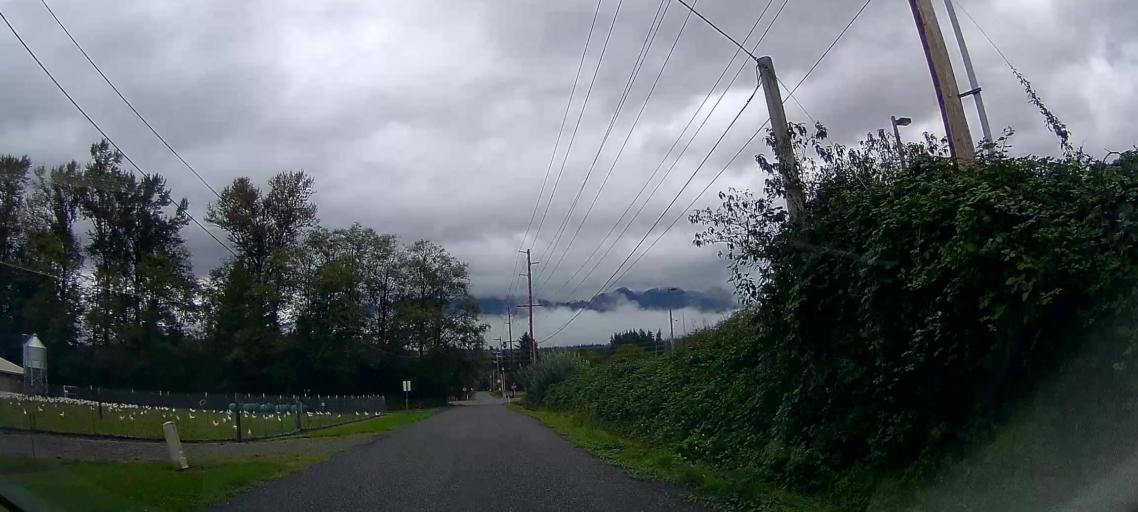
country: US
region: Washington
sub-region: Skagit County
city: Sedro-Woolley
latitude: 48.5294
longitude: -122.0061
